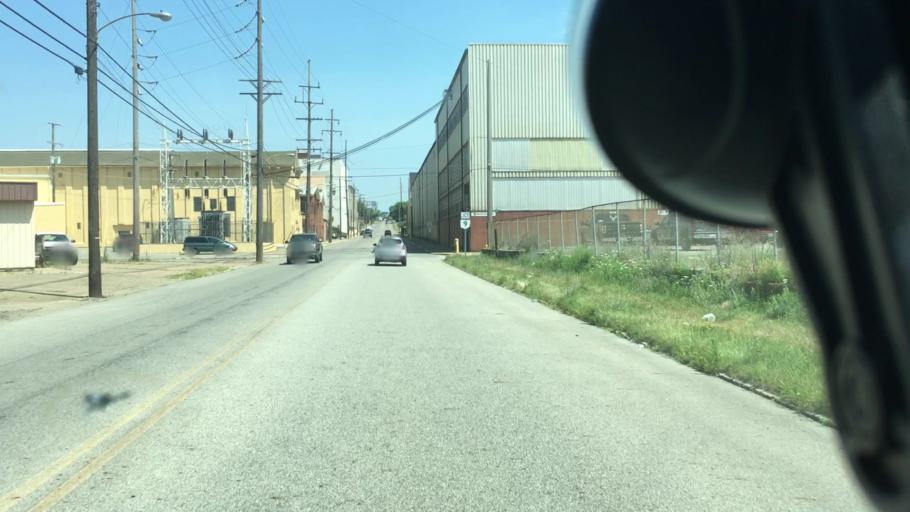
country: US
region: Ohio
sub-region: Columbiana County
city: Salem
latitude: 40.8933
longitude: -80.8568
